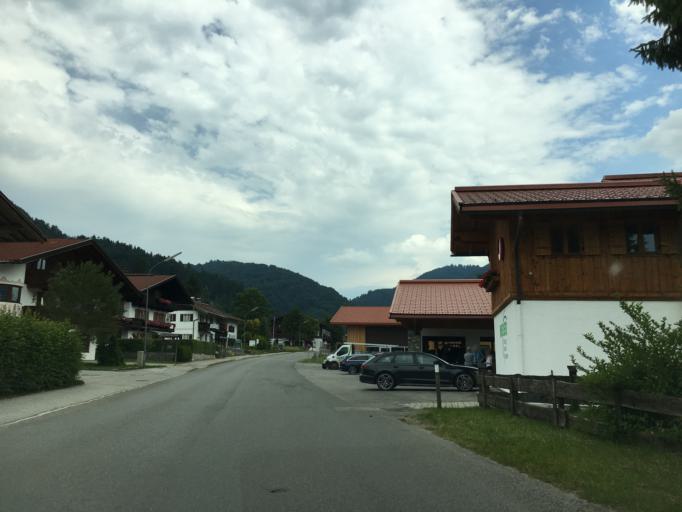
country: DE
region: Bavaria
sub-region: Upper Bavaria
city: Reit im Winkl
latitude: 47.6757
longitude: 12.4830
